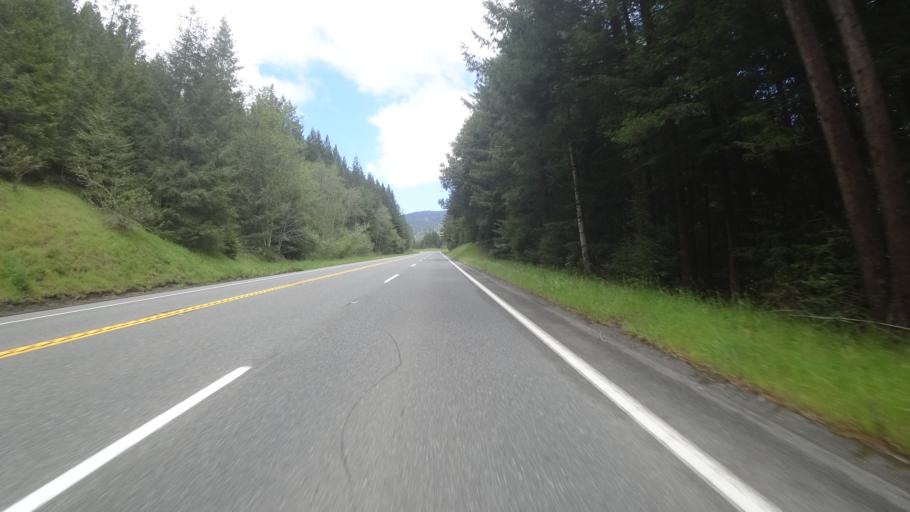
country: US
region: California
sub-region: Humboldt County
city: Blue Lake
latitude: 40.9347
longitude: -123.9003
